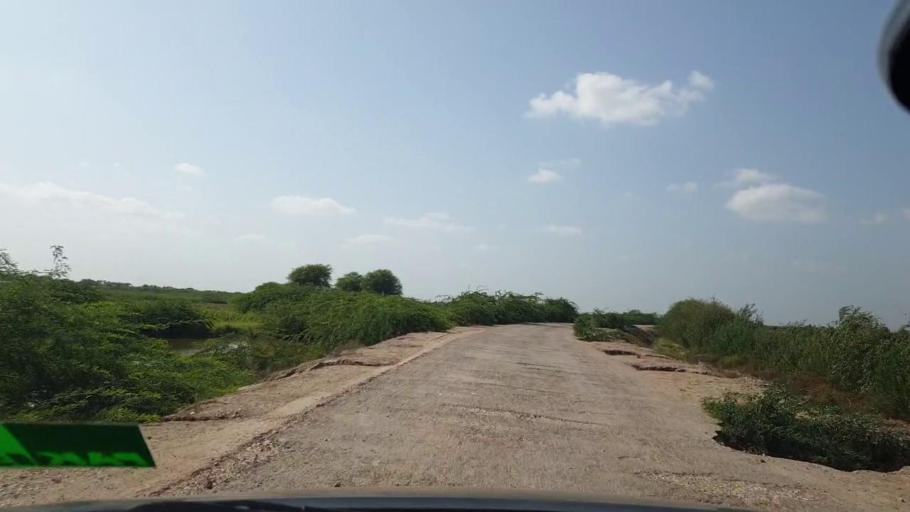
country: PK
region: Sindh
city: Tando Bago
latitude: 24.6654
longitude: 69.1981
